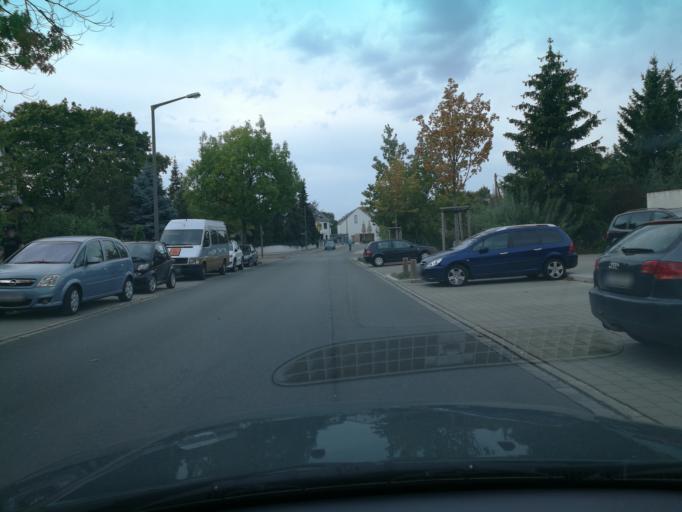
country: DE
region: Bavaria
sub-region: Regierungsbezirk Mittelfranken
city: Wetzendorf
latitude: 49.4674
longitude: 11.0489
